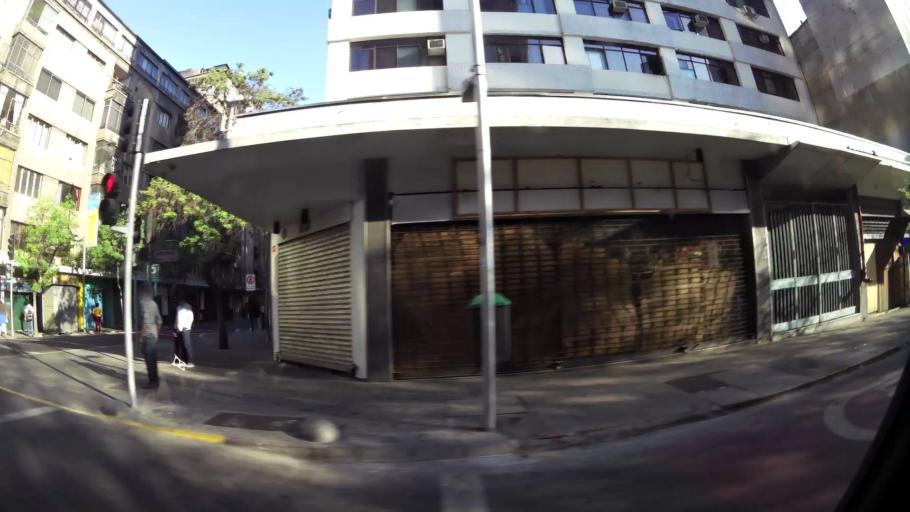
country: CL
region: Santiago Metropolitan
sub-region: Provincia de Santiago
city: Santiago
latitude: -33.4360
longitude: -70.6488
